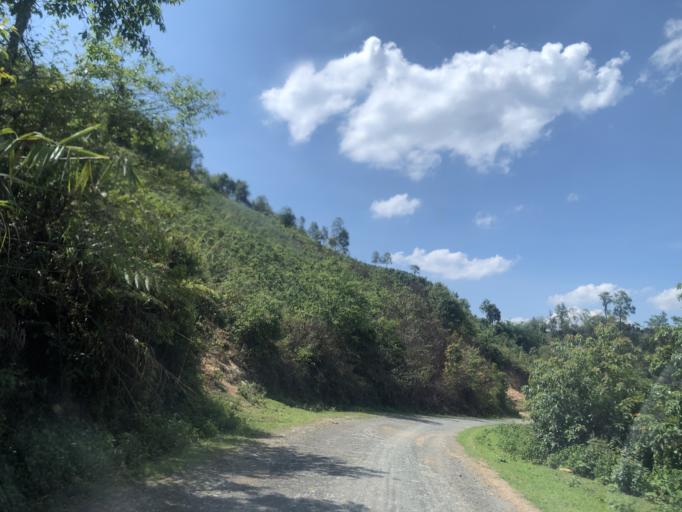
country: LA
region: Phongsali
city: Phongsali
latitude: 21.4187
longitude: 102.2512
